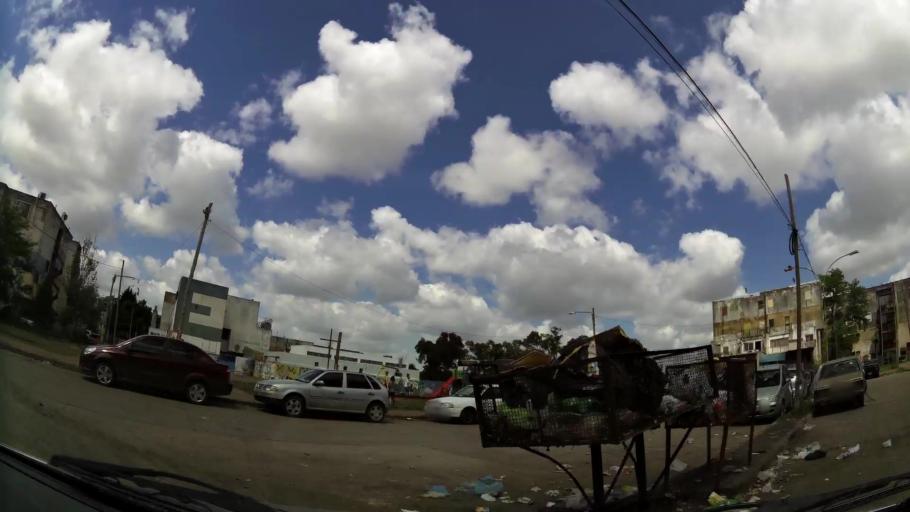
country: AR
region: Buenos Aires
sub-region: Partido de Quilmes
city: Quilmes
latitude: -34.8327
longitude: -58.2225
